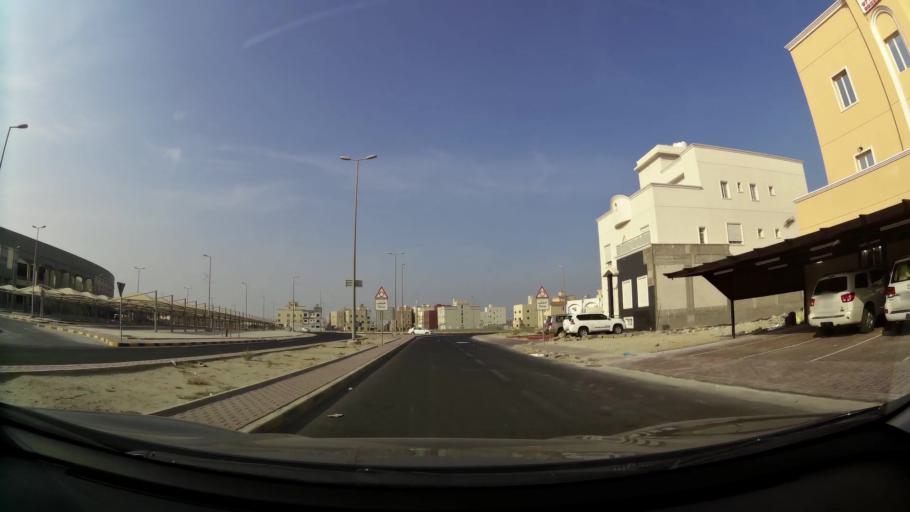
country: KW
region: Mubarak al Kabir
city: Mubarak al Kabir
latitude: 29.1965
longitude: 48.1030
